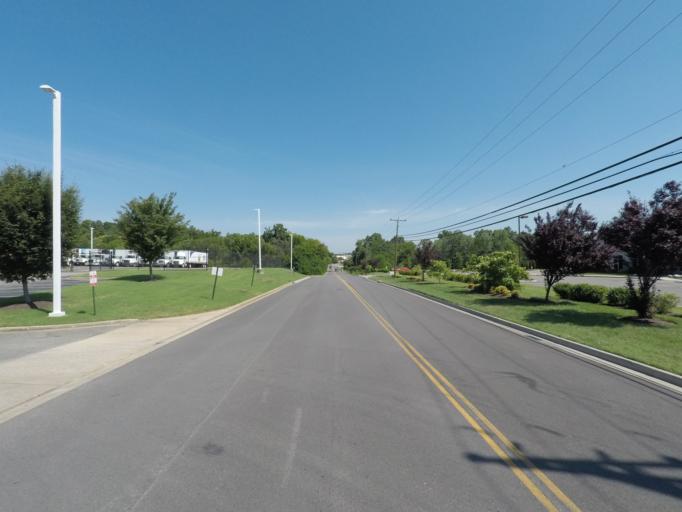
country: US
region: Virginia
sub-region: Henrico County
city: Dumbarton
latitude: 37.5875
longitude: -77.4843
